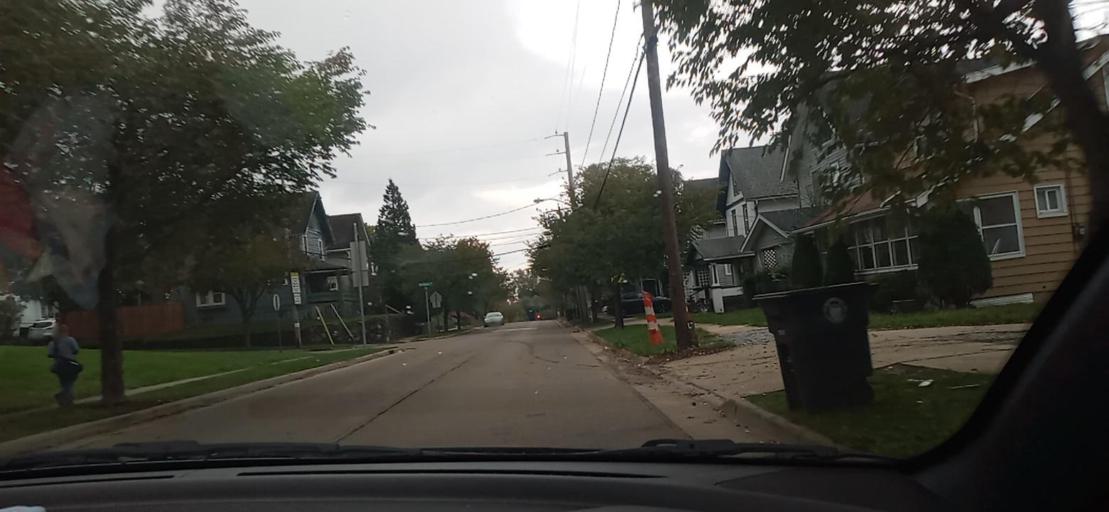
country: US
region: Ohio
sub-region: Summit County
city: Portage Lakes
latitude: 41.0455
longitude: -81.5605
